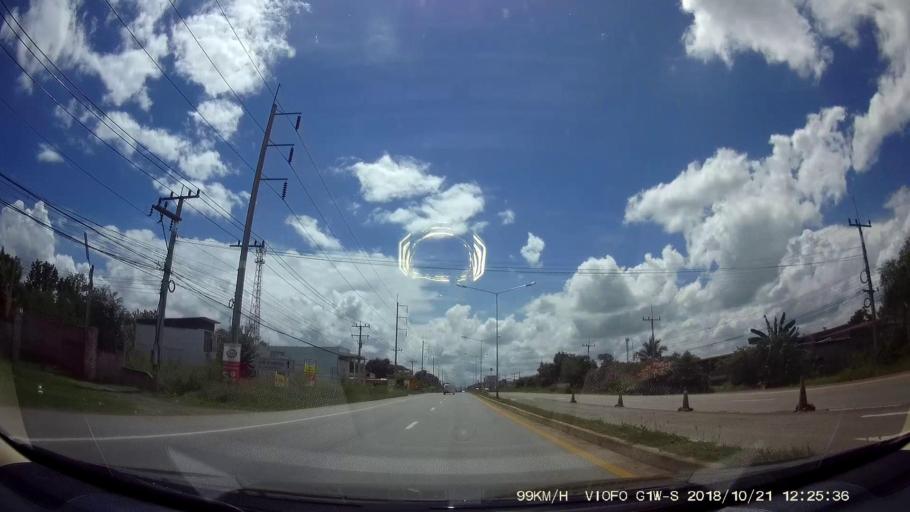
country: TH
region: Nakhon Ratchasima
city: Dan Khun Thot
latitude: 15.2191
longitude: 101.7710
